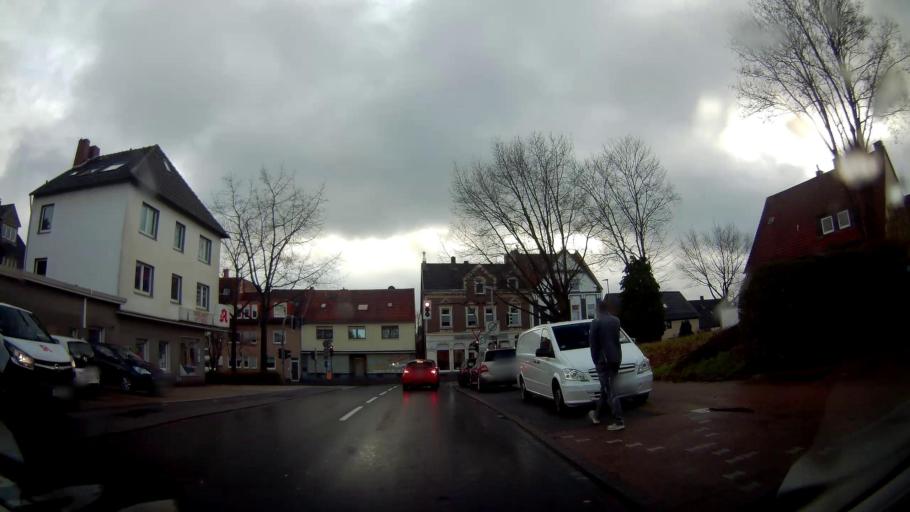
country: DE
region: North Rhine-Westphalia
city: Castrop-Rauxel
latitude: 51.5010
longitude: 7.2839
